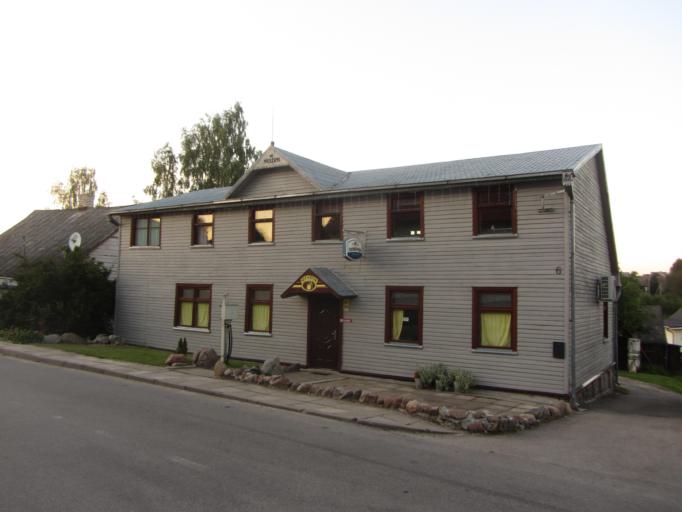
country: LT
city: Sakiai
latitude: 55.0787
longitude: 23.2733
